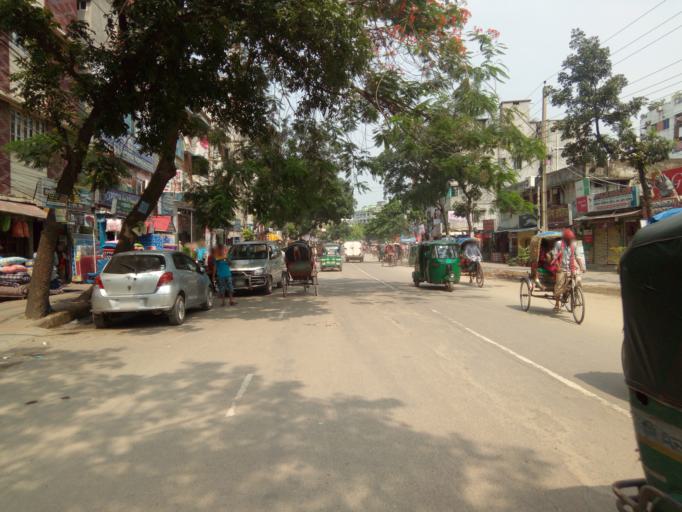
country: BD
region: Dhaka
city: Paltan
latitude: 23.7518
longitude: 90.4228
